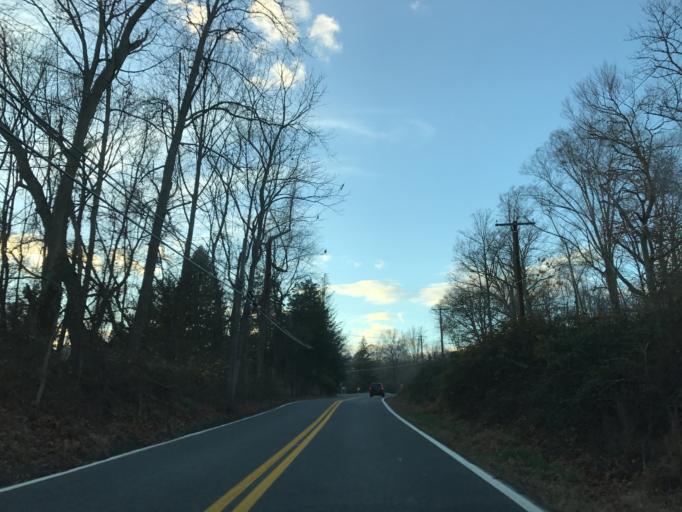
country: US
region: Maryland
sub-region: Cecil County
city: Rising Sun
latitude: 39.6799
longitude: -76.2225
